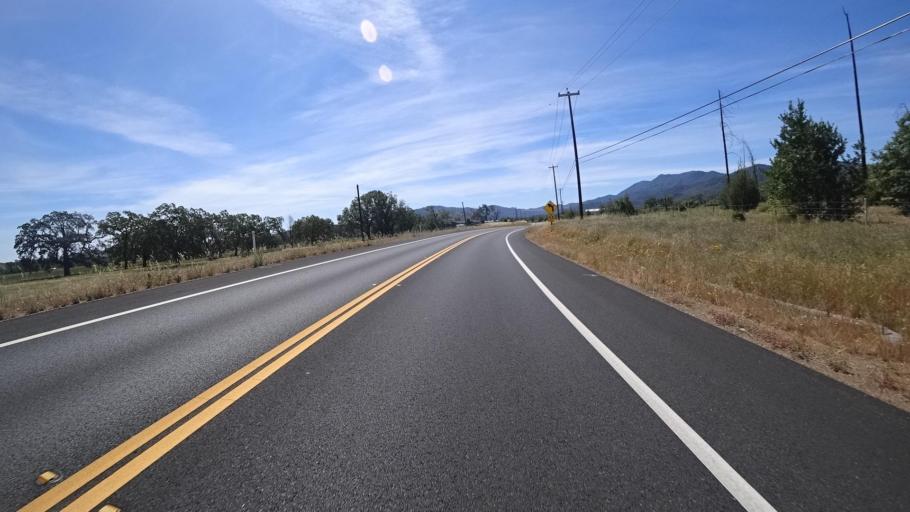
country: US
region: California
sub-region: Lake County
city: Middletown
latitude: 38.7621
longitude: -122.6430
